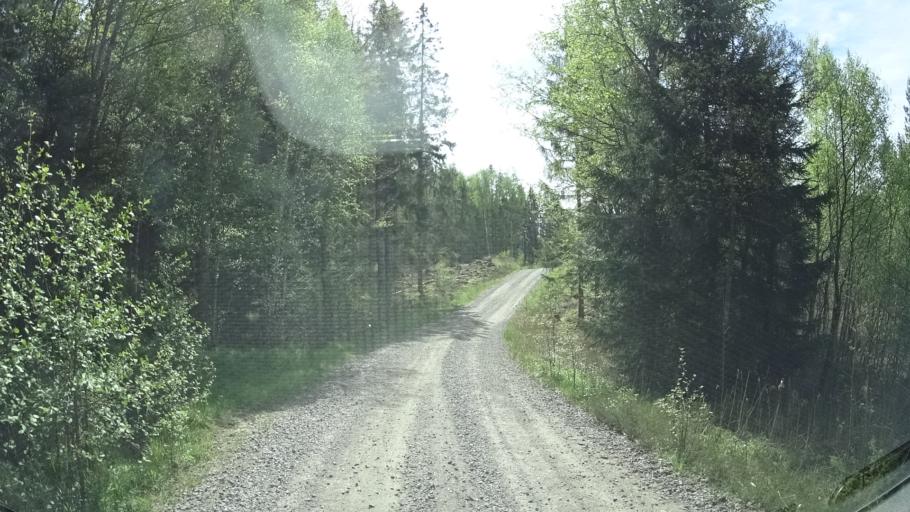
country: SE
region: OEstergoetland
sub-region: Finspangs Kommun
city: Finspang
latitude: 58.7875
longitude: 15.8465
